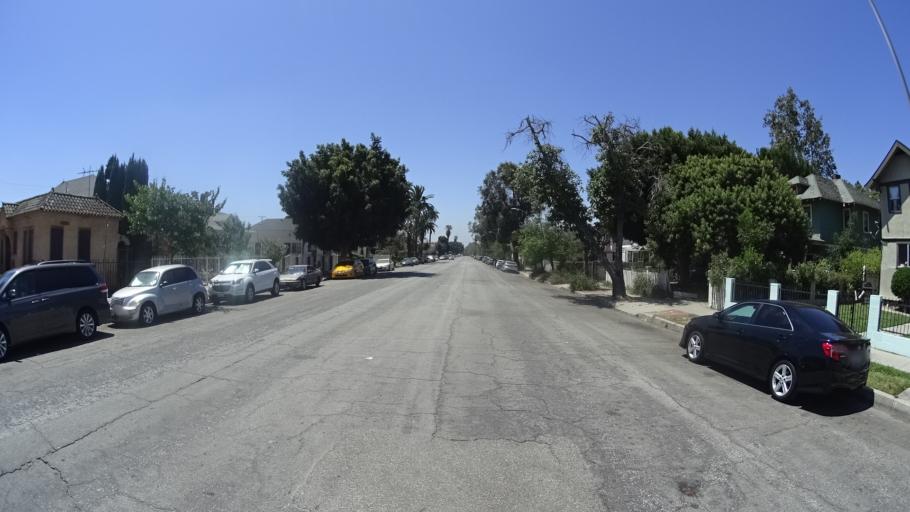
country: US
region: California
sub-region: Los Angeles County
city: View Park-Windsor Hills
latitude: 34.0322
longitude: -118.3028
